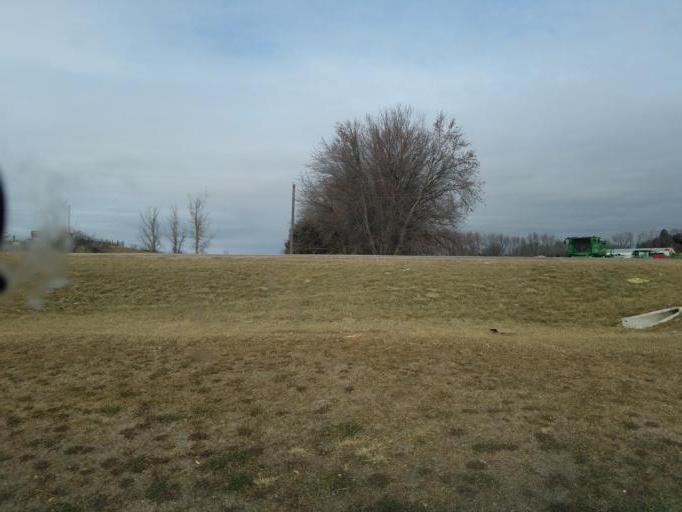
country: US
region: Nebraska
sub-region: Knox County
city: Bloomfield
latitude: 42.5995
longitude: -97.6571
